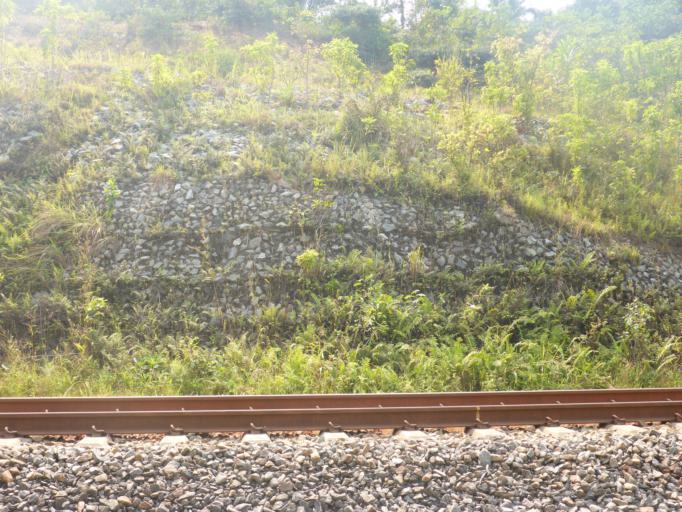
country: SL
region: Northern Province
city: Bumbuna
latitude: 8.9451
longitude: -11.7429
